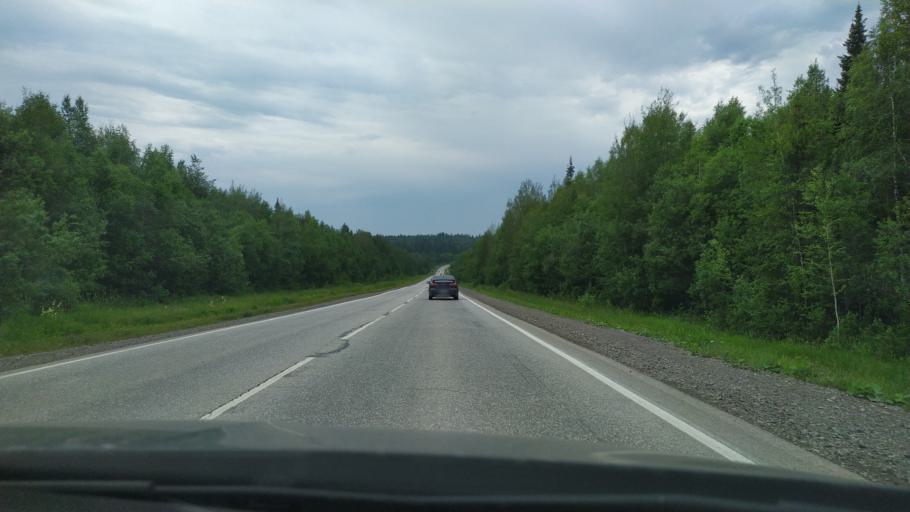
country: RU
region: Perm
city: Chusovoy
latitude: 58.3786
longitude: 57.8941
